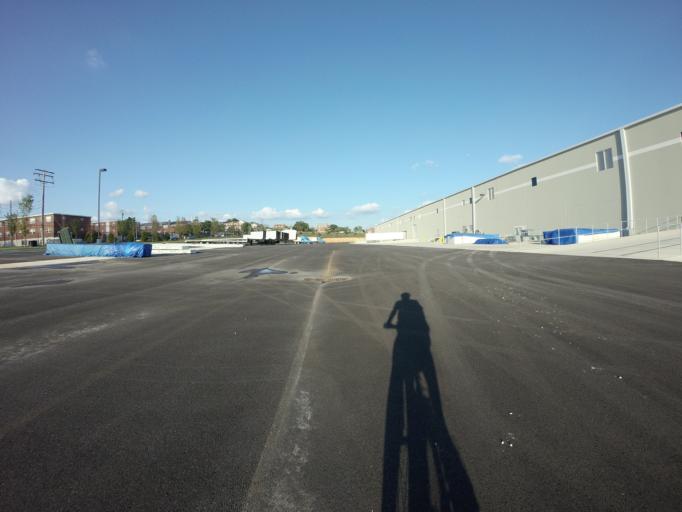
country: US
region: Maryland
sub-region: Baltimore County
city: Dundalk
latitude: 39.2758
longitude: -76.5464
